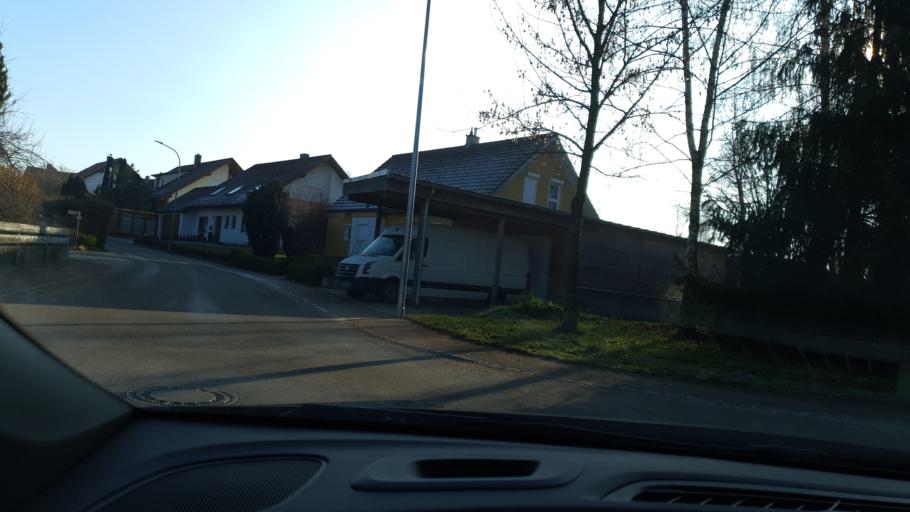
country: DE
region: Bavaria
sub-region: Swabia
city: Burgau
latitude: 48.4289
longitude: 10.3988
